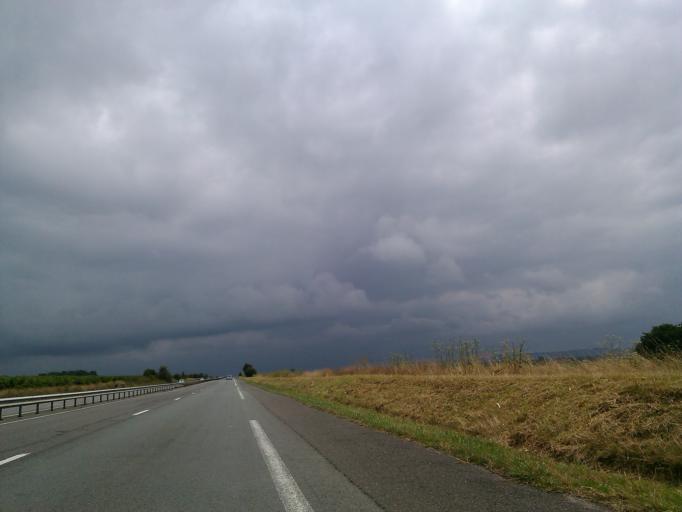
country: FR
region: Poitou-Charentes
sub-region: Departement de la Charente
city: Gensac-la-Pallue
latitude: 45.6695
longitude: -0.2523
